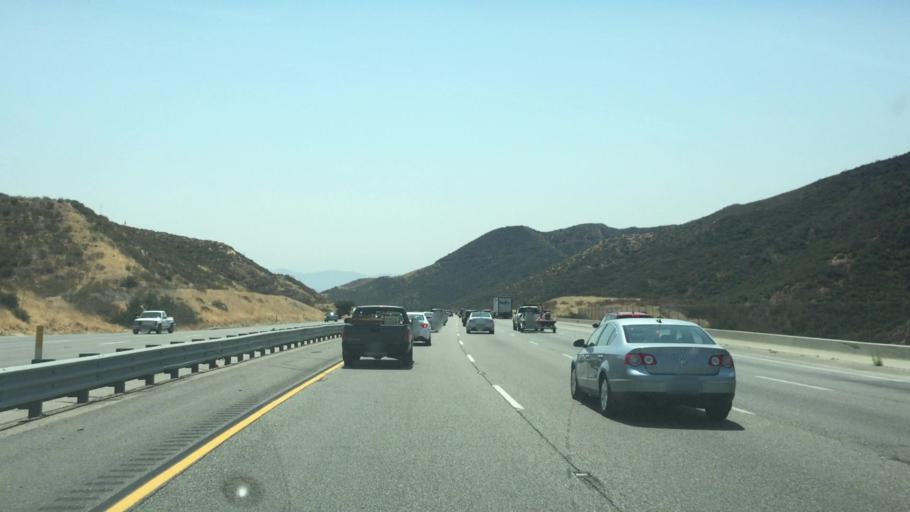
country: US
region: California
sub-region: Los Angeles County
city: Castaic
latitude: 34.5796
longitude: -118.7028
